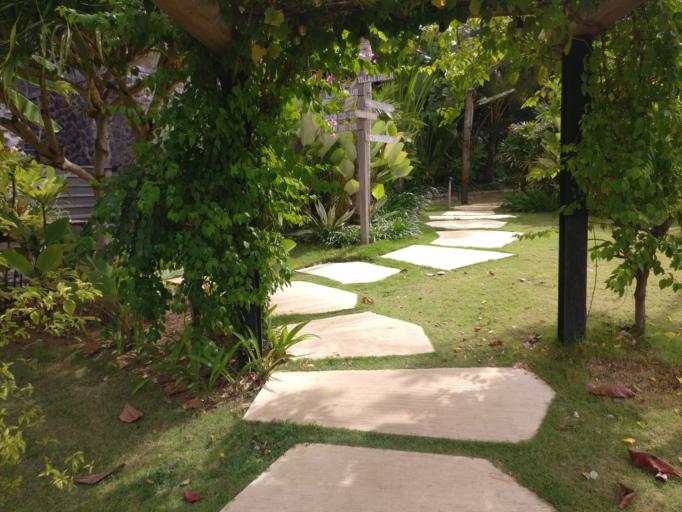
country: ID
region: Bali
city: Banjar Pasekan
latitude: -8.5974
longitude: 115.3381
